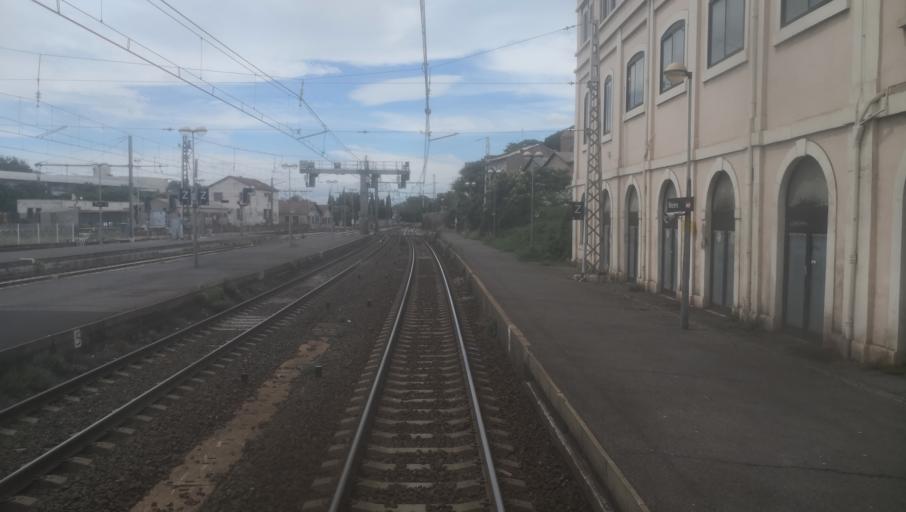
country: FR
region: Languedoc-Roussillon
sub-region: Departement de l'Herault
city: Beziers
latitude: 43.3365
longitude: 3.2171
